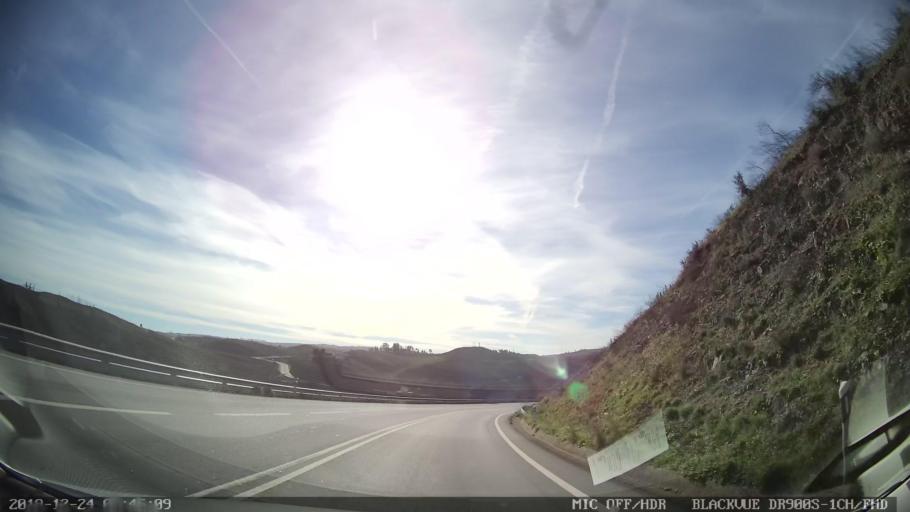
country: PT
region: Portalegre
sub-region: Nisa
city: Nisa
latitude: 39.5471
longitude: -7.7982
